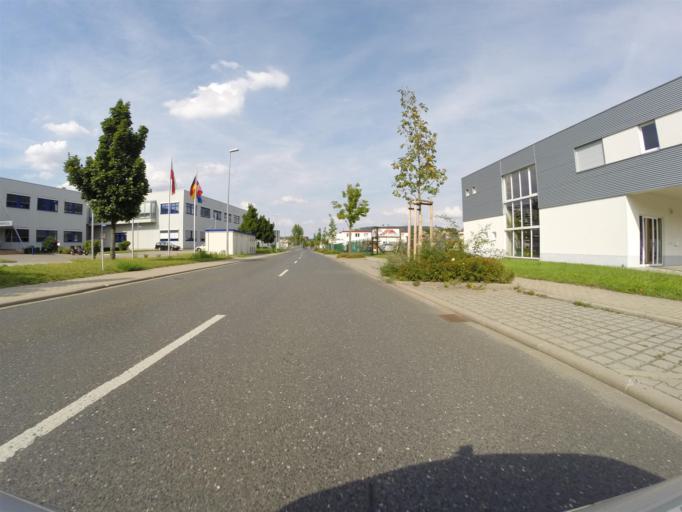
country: DE
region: Thuringia
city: Jena
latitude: 50.9441
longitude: 11.6061
